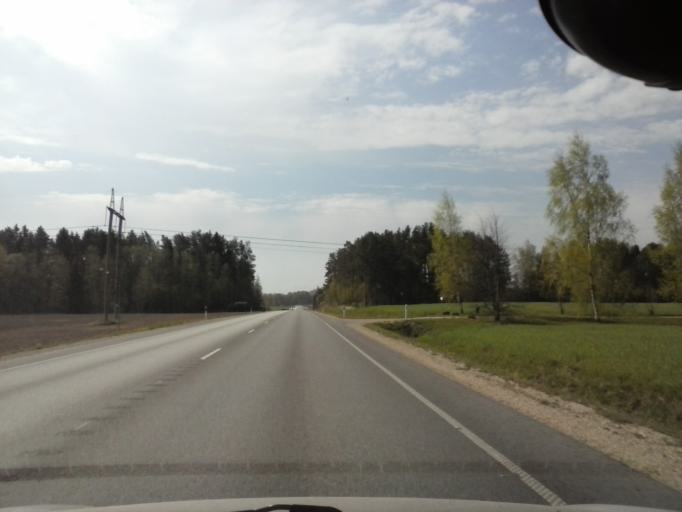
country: EE
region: Tartu
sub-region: UElenurme vald
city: Ulenurme
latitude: 58.2162
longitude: 26.7041
